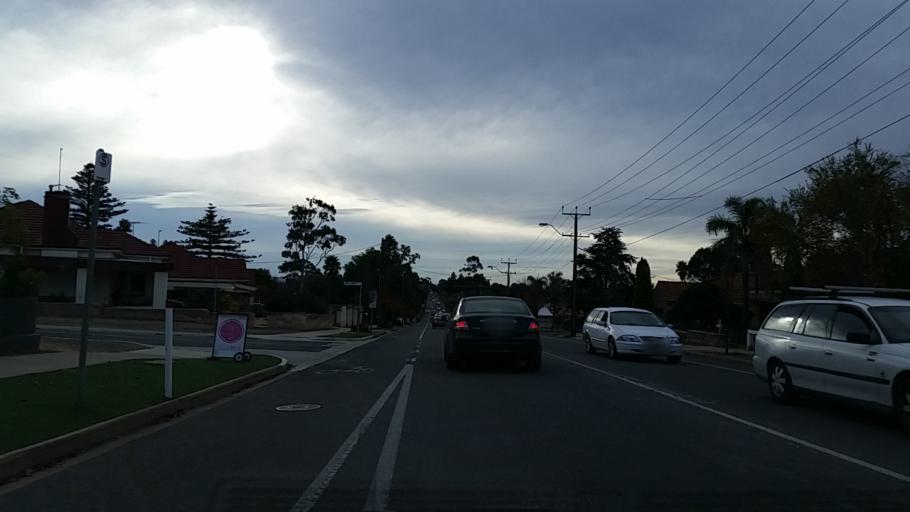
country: AU
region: South Australia
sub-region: Murray Bridge
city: Murray Bridge
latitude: -35.1280
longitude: 139.2790
